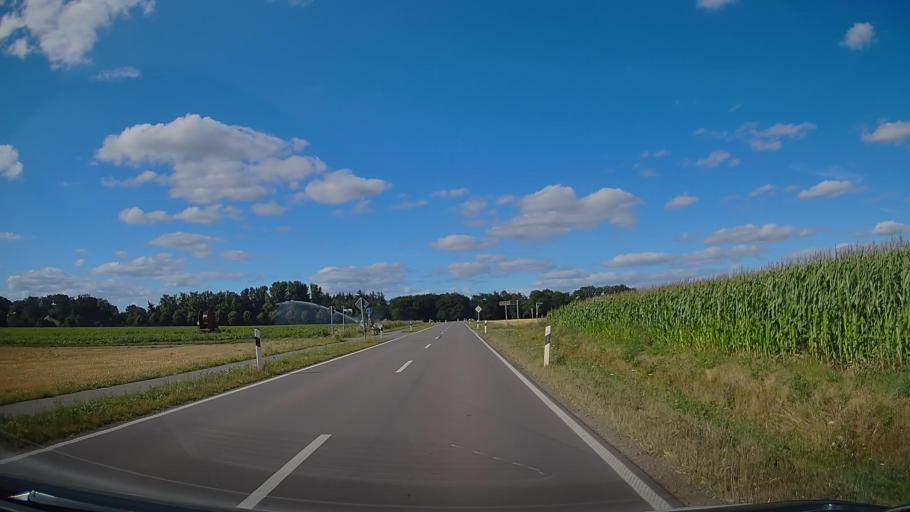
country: DE
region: Lower Saxony
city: Loningen
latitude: 52.7185
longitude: 7.7502
